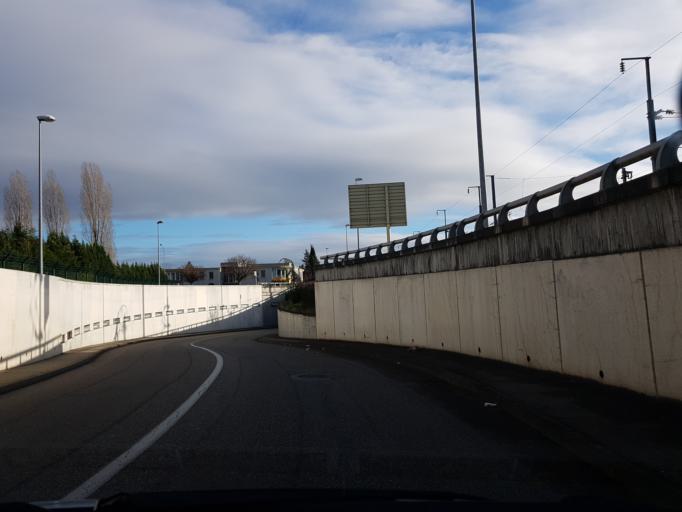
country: FR
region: Alsace
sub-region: Departement du Haut-Rhin
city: Habsheim
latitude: 47.7412
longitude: 7.4156
